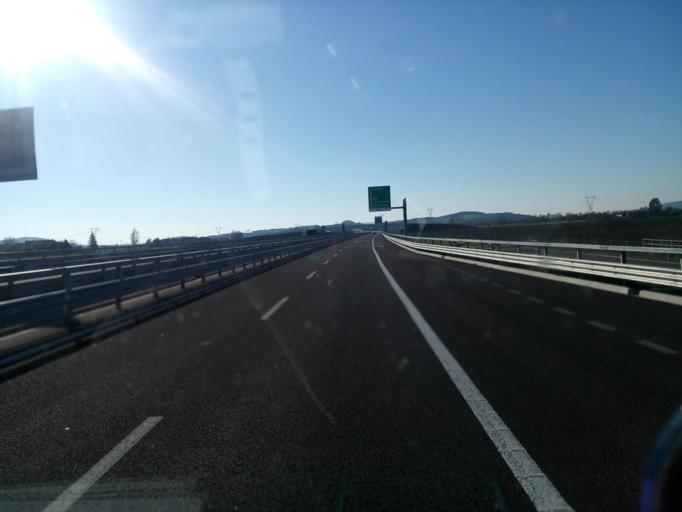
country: IT
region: Veneto
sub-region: Provincia di Padova
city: Bastia
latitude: 45.3968
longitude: 11.6249
